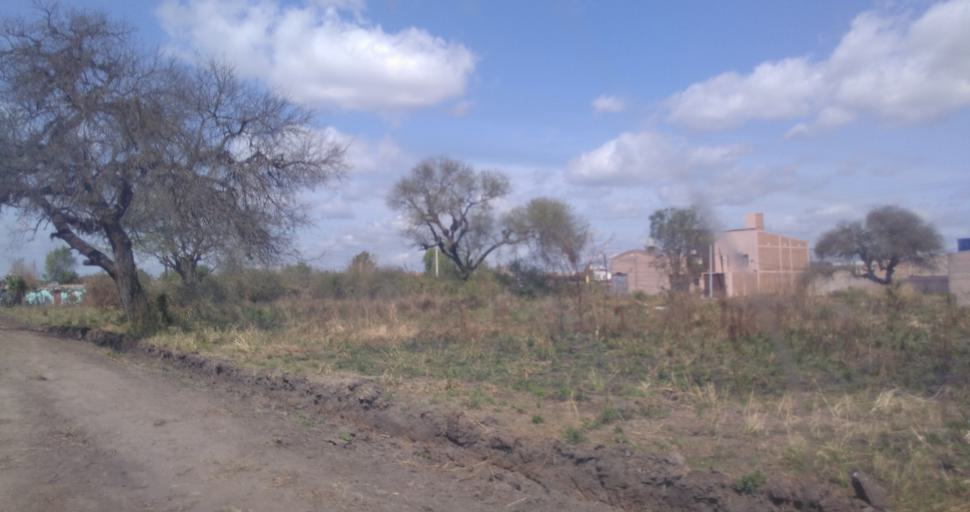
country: AR
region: Chaco
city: Fontana
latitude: -27.4290
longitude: -59.0228
